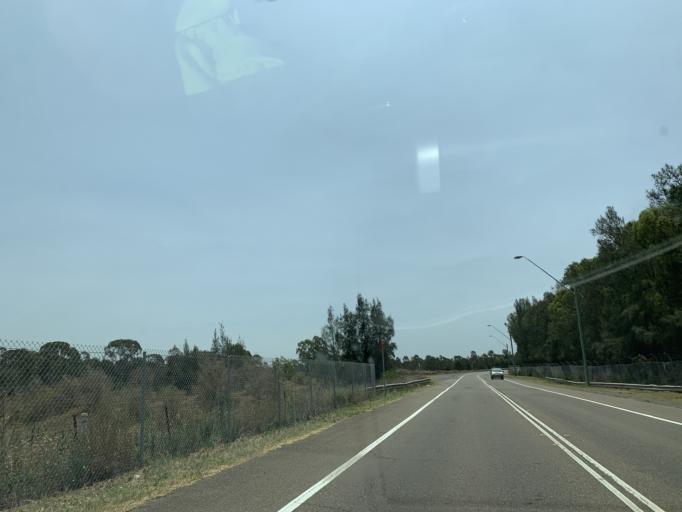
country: AU
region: New South Wales
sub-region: Blacktown
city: Doonside
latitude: -33.8046
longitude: 150.8643
